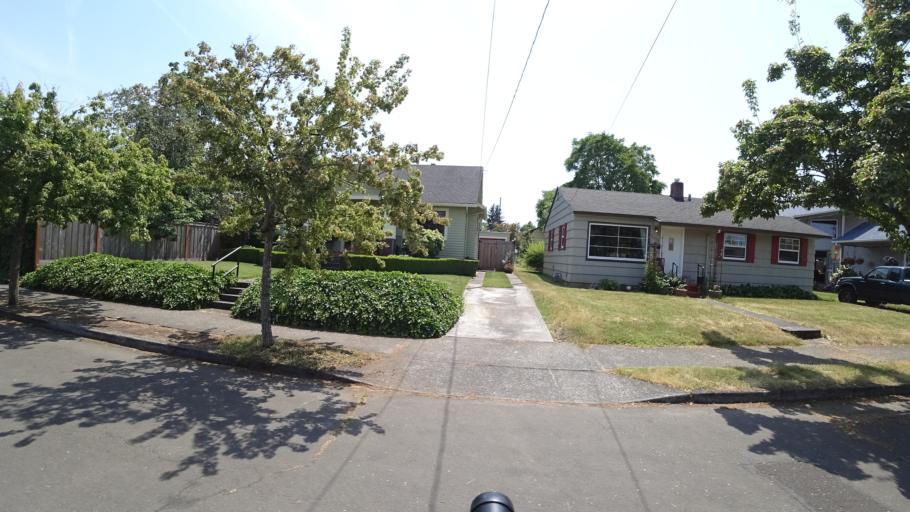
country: US
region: Oregon
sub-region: Multnomah County
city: Portland
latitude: 45.5785
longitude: -122.6908
